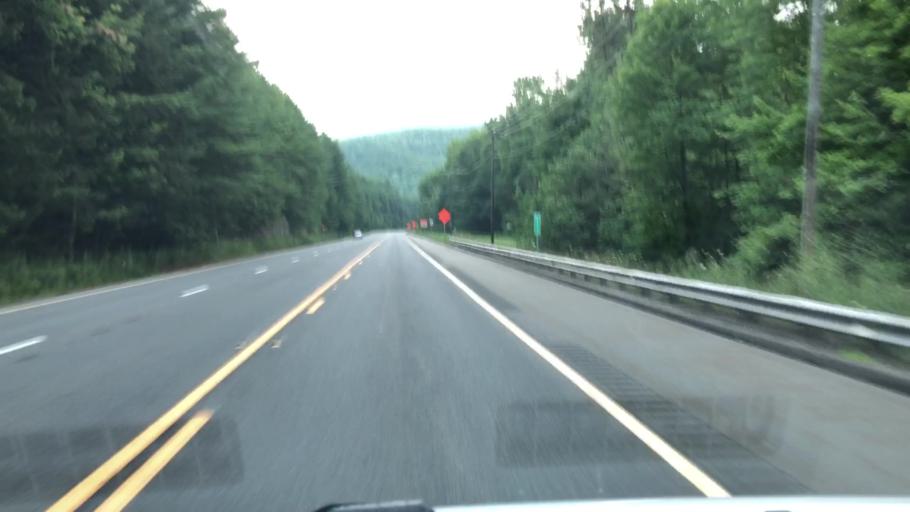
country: US
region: Massachusetts
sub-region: Berkshire County
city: Hinsdale
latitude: 42.4854
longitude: -72.9798
